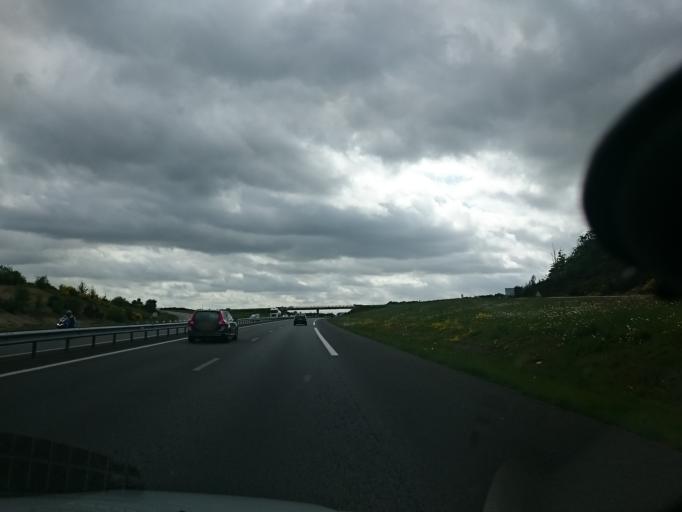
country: FR
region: Brittany
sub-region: Departement d'Ille-et-Vilaine
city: Saint-Aubin-du-Cormier
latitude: 48.2655
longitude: -1.4086
